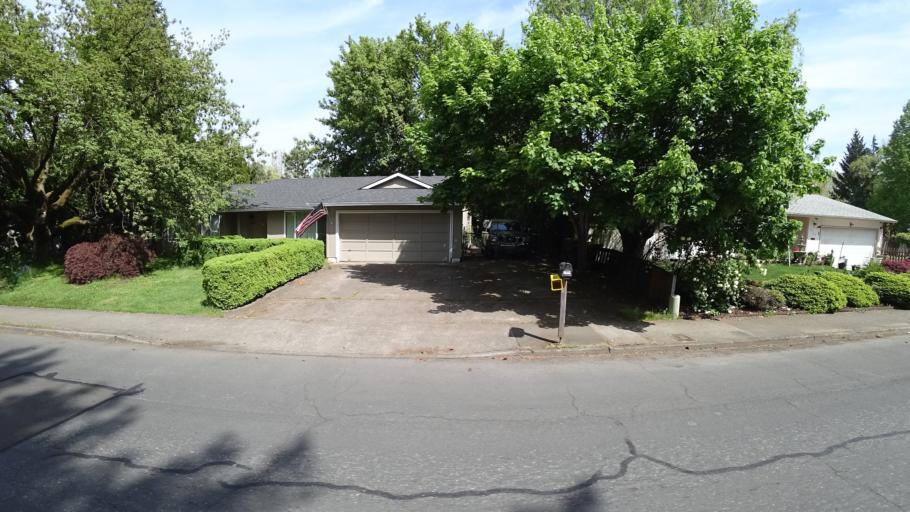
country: US
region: Oregon
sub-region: Washington County
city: Hillsboro
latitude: 45.5280
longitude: -122.9566
